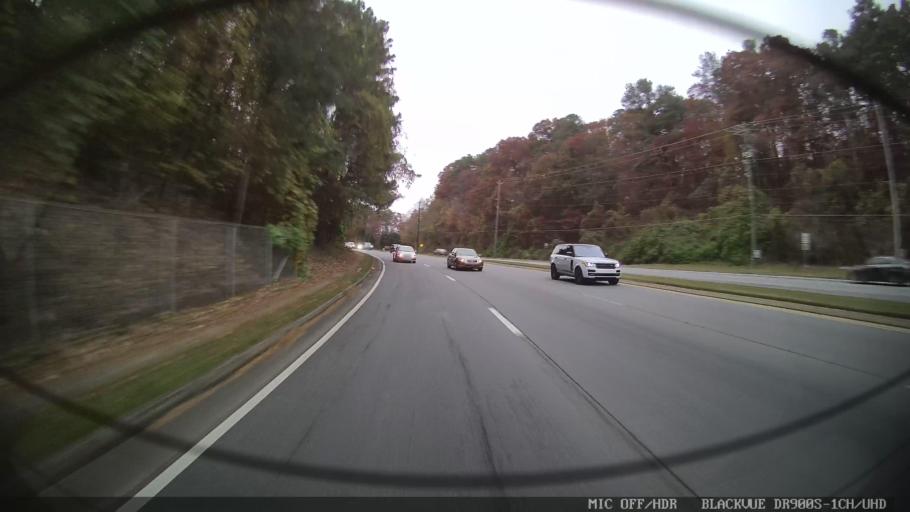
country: US
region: Georgia
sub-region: Fulton County
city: Sandy Springs
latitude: 33.9472
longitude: -84.4074
